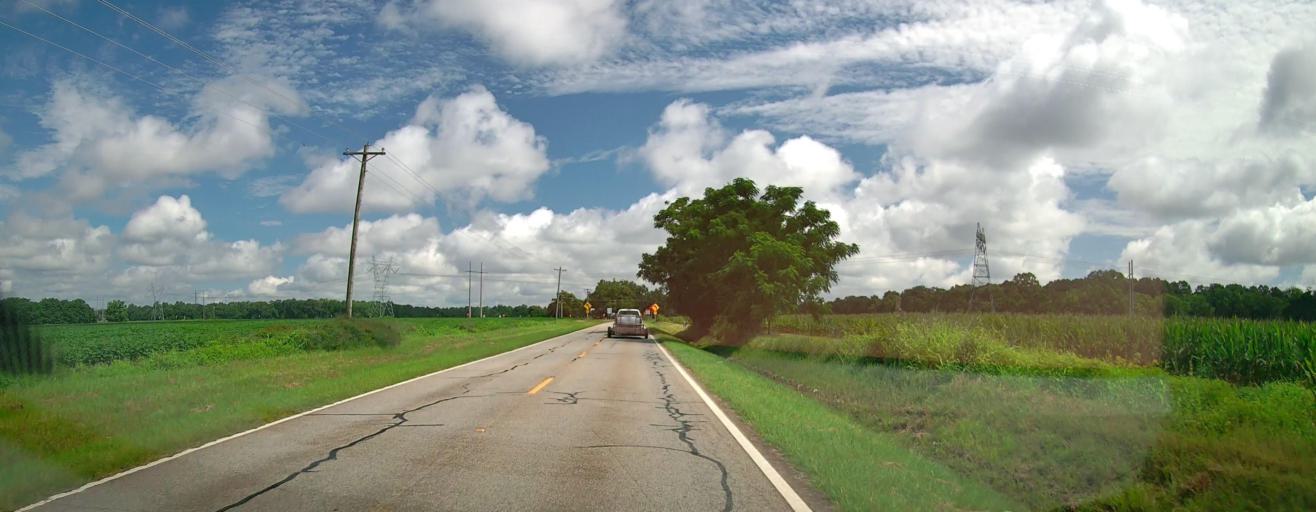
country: US
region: Georgia
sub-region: Peach County
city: Byron
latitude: 32.6610
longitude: -83.8053
